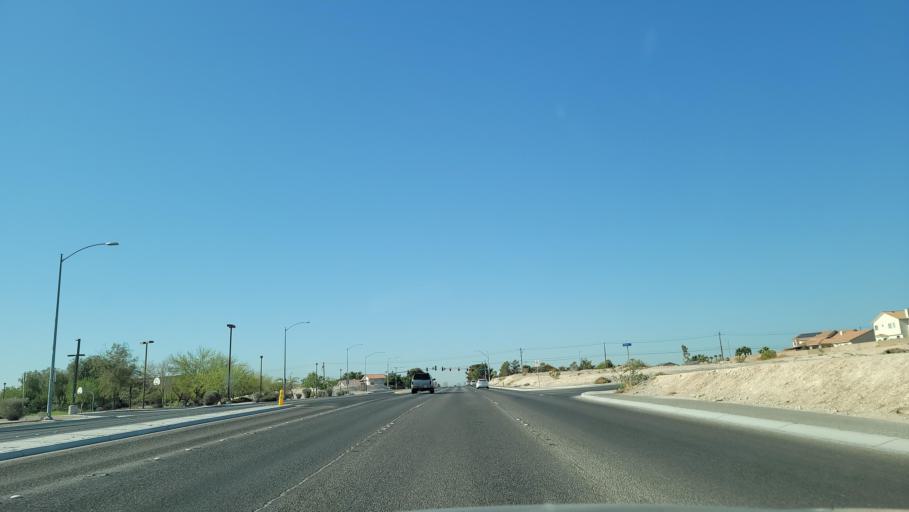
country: US
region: Nevada
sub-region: Clark County
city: Las Vegas
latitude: 36.2272
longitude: -115.1800
